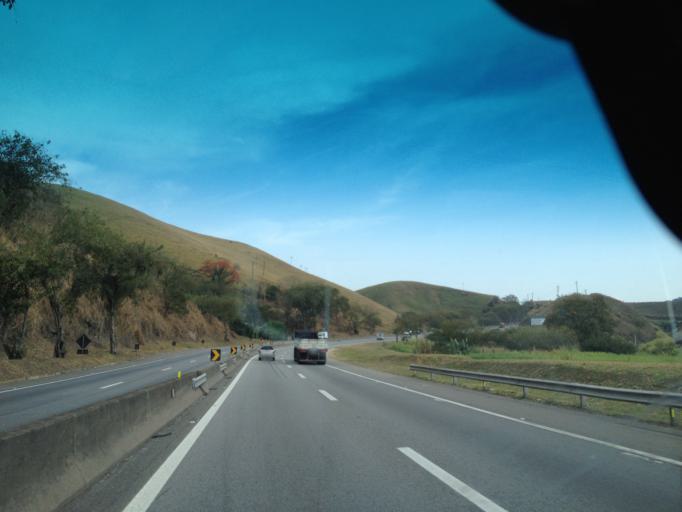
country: BR
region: Rio de Janeiro
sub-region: Porto Real
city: Porto Real
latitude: -22.4830
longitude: -44.2592
